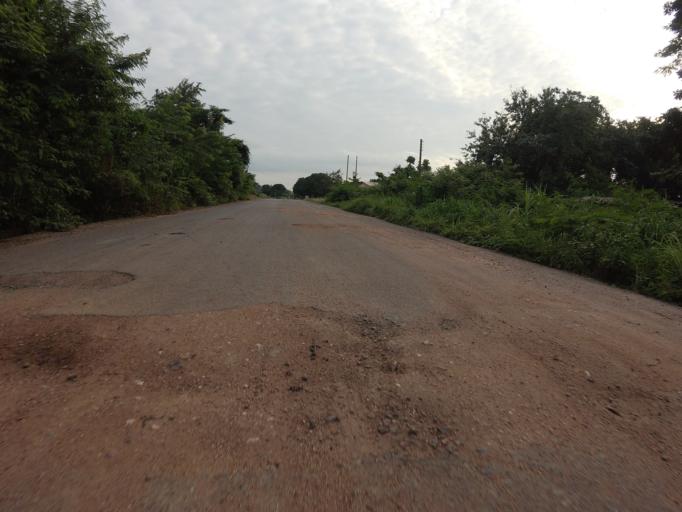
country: GH
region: Volta
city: Kpandu
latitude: 6.8661
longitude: 0.4014
